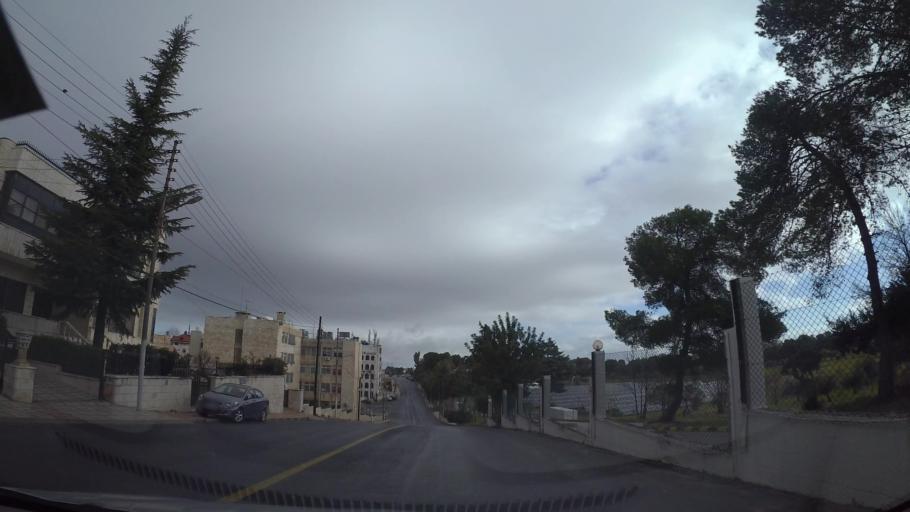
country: JO
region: Amman
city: Al Jubayhah
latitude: 32.0266
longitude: 35.8775
